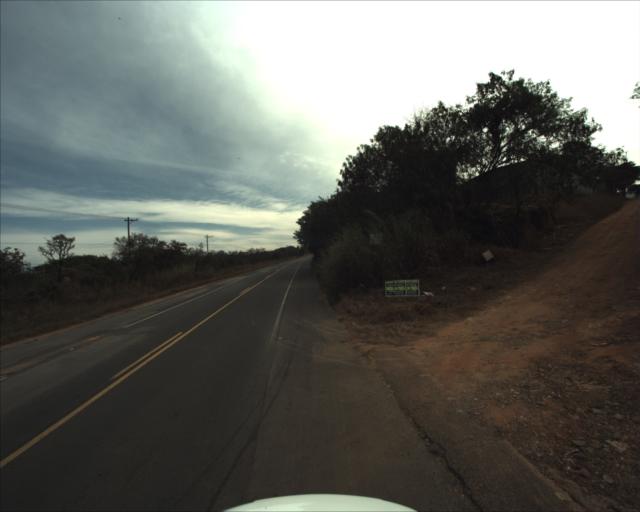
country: BR
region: Sao Paulo
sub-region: Sorocaba
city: Sorocaba
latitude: -23.3719
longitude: -47.5307
